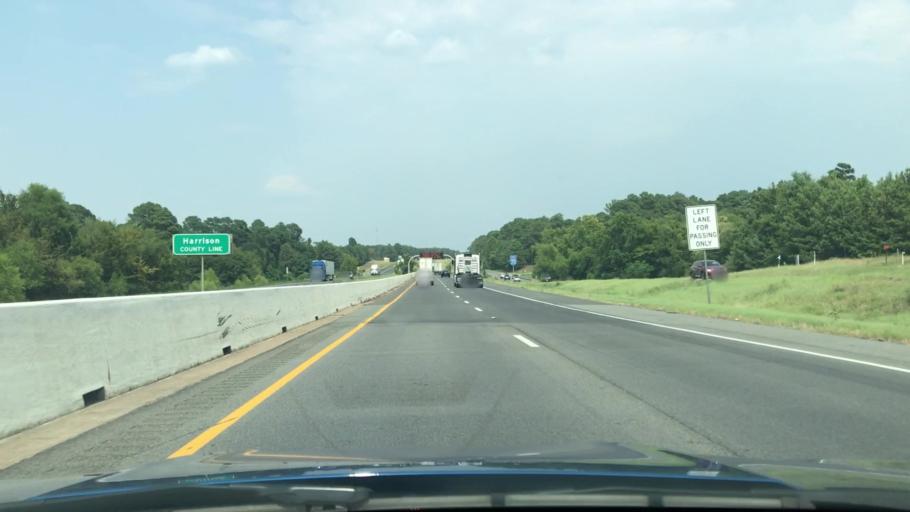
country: US
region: Texas
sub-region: Gregg County
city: Longview
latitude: 32.4523
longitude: -94.7027
